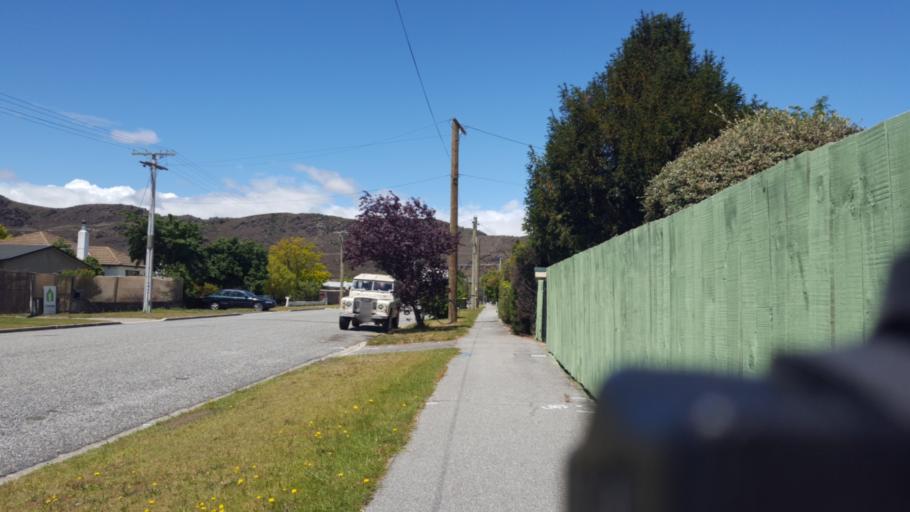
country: NZ
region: Otago
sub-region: Queenstown-Lakes District
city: Wanaka
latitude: -45.2507
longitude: 169.3931
